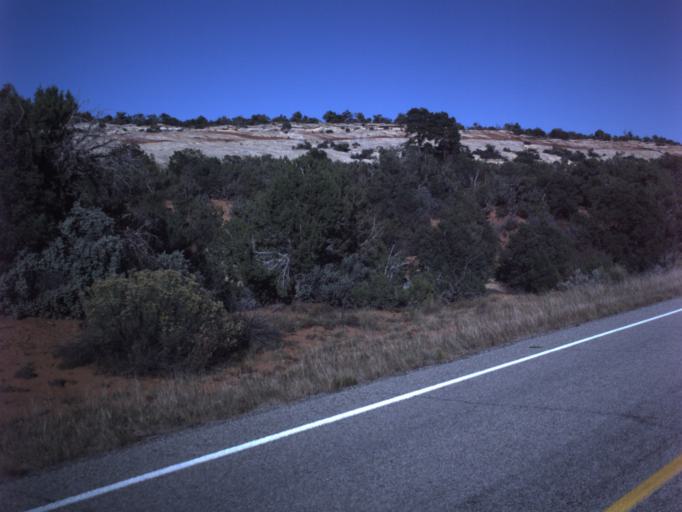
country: US
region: Utah
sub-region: San Juan County
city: Blanding
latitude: 37.5443
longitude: -109.7613
